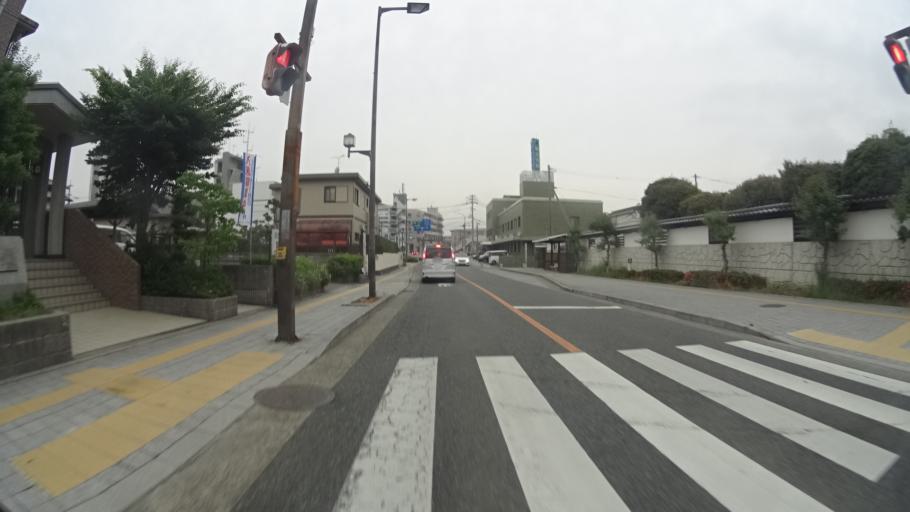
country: JP
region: Fukuoka
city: Dazaifu
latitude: 33.5132
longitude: 130.5095
